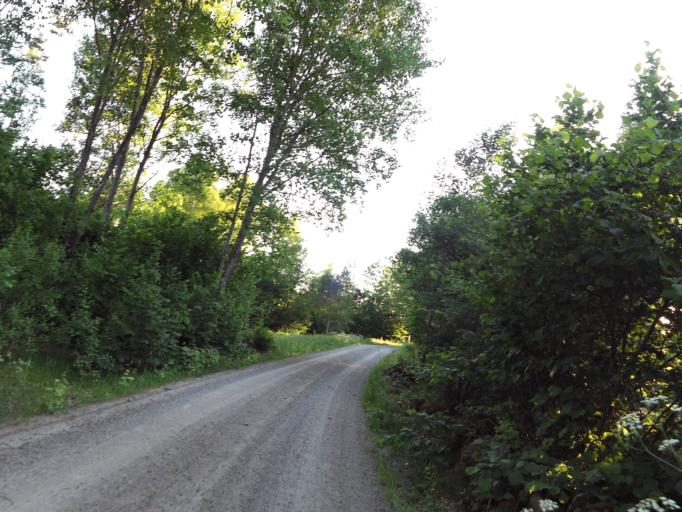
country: SE
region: Blekinge
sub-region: Olofstroms Kommun
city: Olofstroem
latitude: 56.4047
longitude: 14.5689
